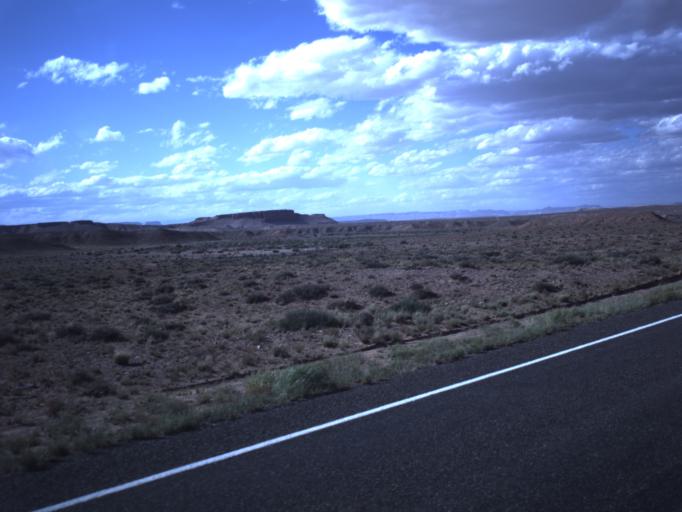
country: US
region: Utah
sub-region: Emery County
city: Ferron
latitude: 38.3082
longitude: -110.6714
